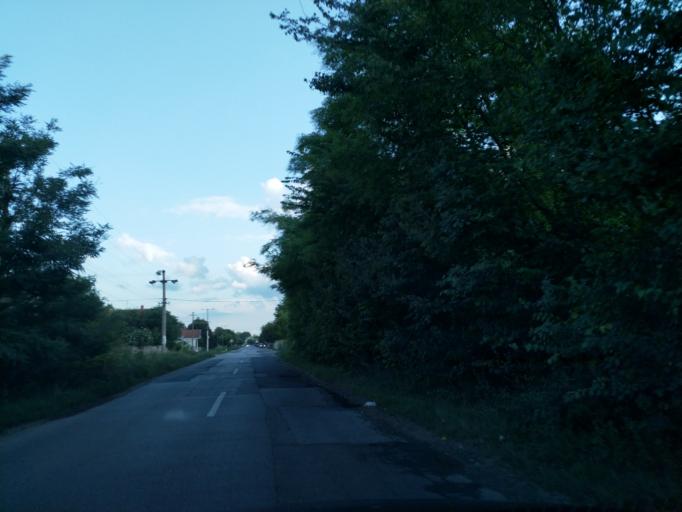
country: RS
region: Central Serbia
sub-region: Rasinski Okrug
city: Cicevac
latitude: 43.7681
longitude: 21.4280
